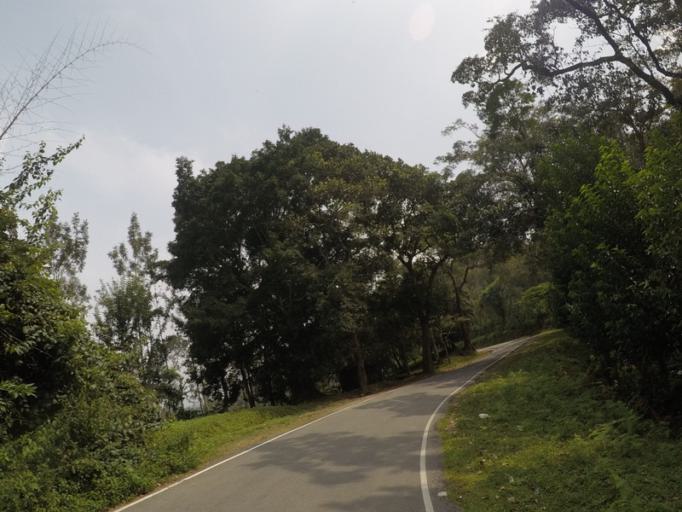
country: IN
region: Karnataka
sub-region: Chikmagalur
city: Mudigere
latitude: 13.1978
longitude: 75.4045
